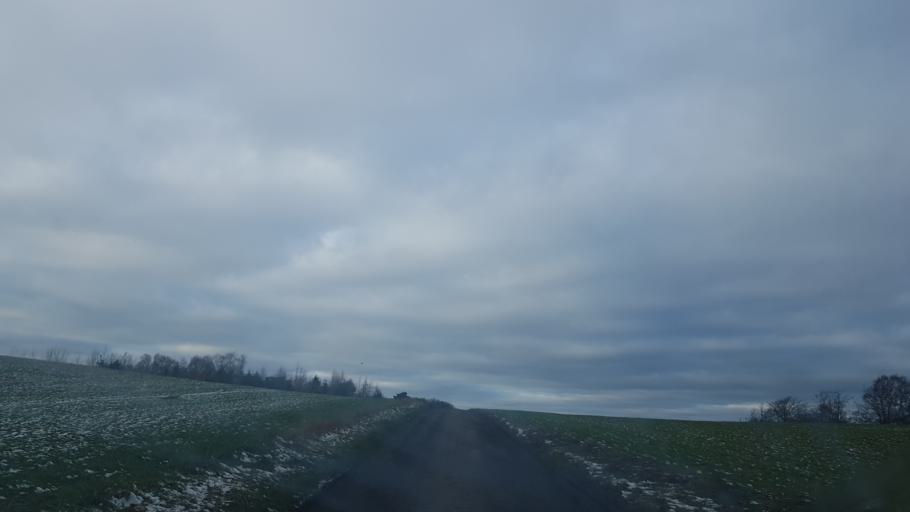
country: DK
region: Zealand
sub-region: Odsherred Kommune
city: Hojby
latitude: 55.9235
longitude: 11.5941
